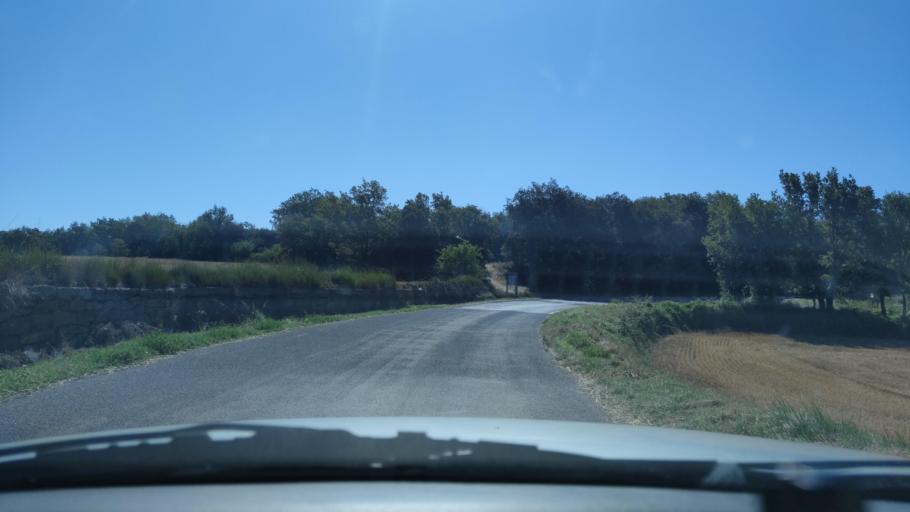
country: ES
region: Catalonia
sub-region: Provincia de Barcelona
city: Cardona
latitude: 41.8892
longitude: 1.5659
